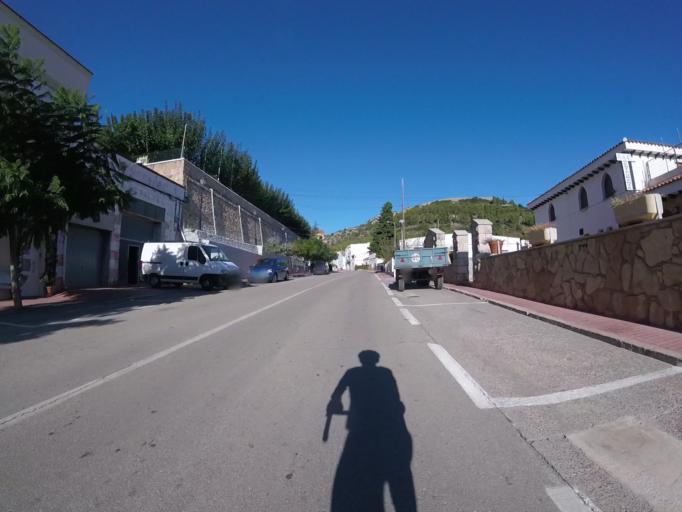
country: ES
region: Valencia
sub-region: Provincia de Castello
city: Cervera del Maestre
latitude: 40.4558
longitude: 0.2753
